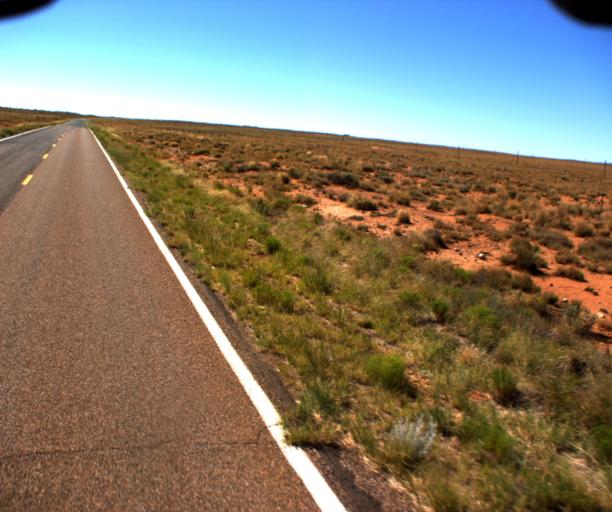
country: US
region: Arizona
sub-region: Coconino County
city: LeChee
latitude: 35.1317
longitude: -110.8811
